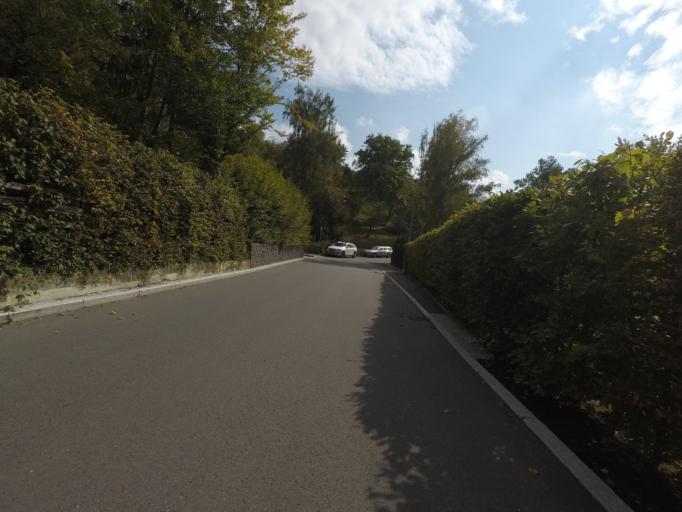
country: DE
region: Baden-Wuerttemberg
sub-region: Tuebingen Region
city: Reutlingen
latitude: 48.4957
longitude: 9.2271
